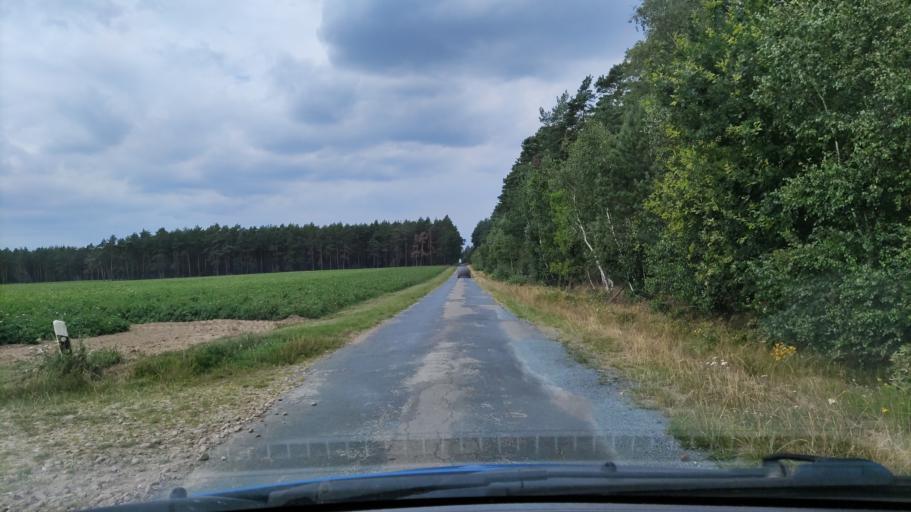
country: DE
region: Lower Saxony
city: Schnega
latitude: 52.9461
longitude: 10.8631
